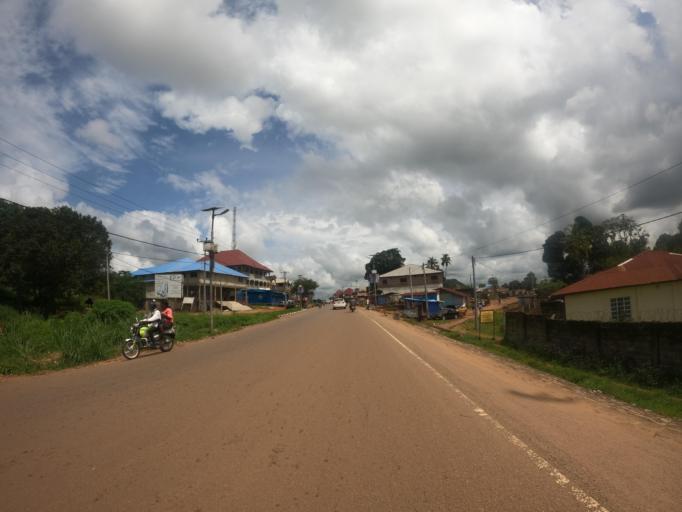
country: SL
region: Northern Province
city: Makeni
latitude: 8.8758
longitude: -12.0504
